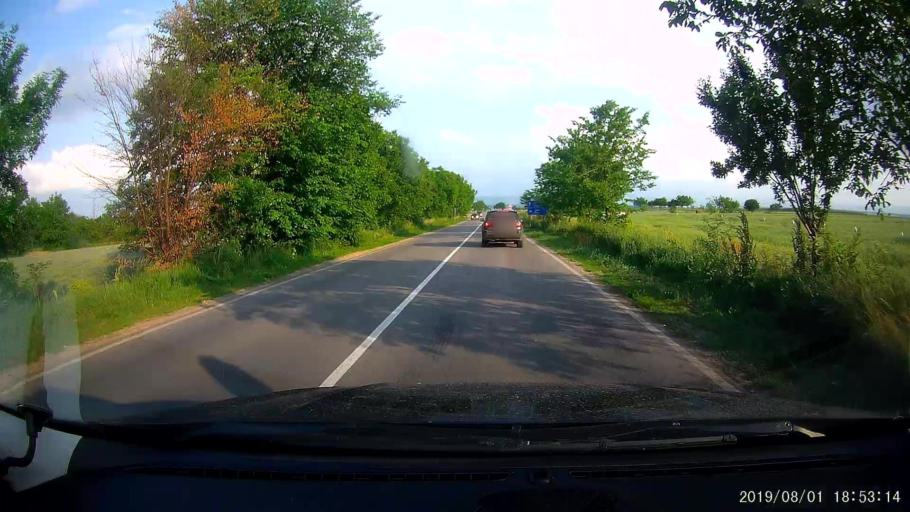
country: BG
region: Shumen
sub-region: Obshtina Shumen
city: Shumen
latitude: 43.2236
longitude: 26.9917
